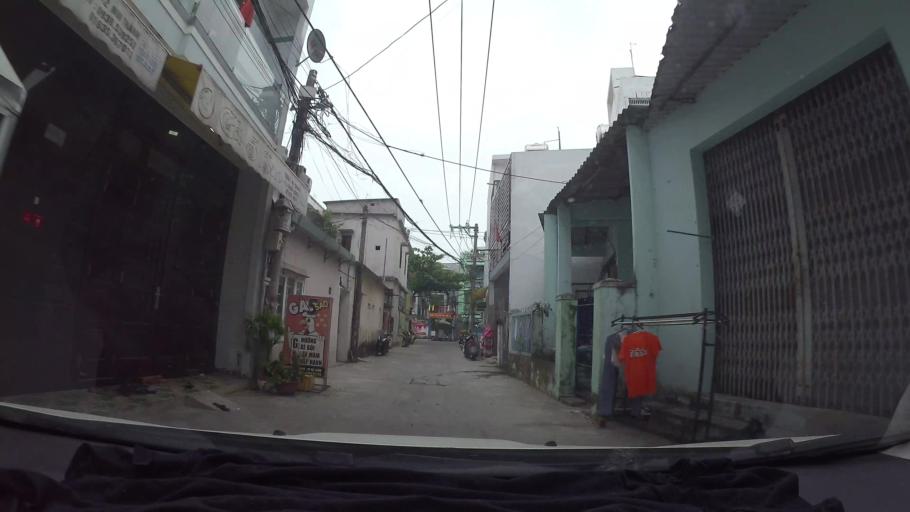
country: VN
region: Da Nang
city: Cam Le
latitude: 16.0314
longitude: 108.2223
